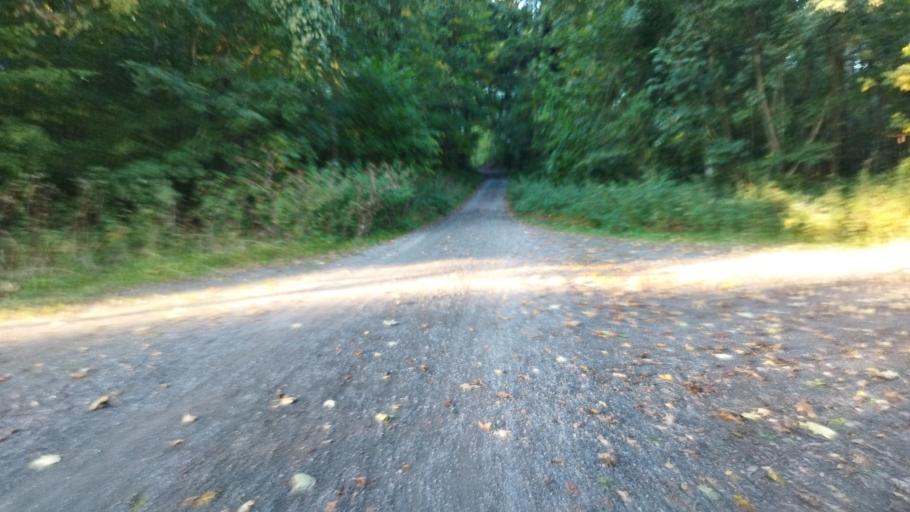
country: DE
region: Baden-Wuerttemberg
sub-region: Regierungsbezirk Stuttgart
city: Cleebronn
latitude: 49.0202
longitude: 9.0272
